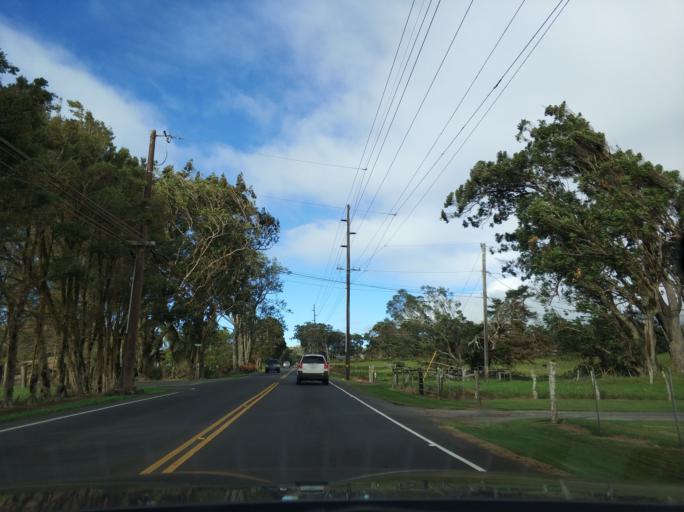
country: US
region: Hawaii
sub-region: Hawaii County
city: Waimea
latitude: 20.0357
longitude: -155.6281
